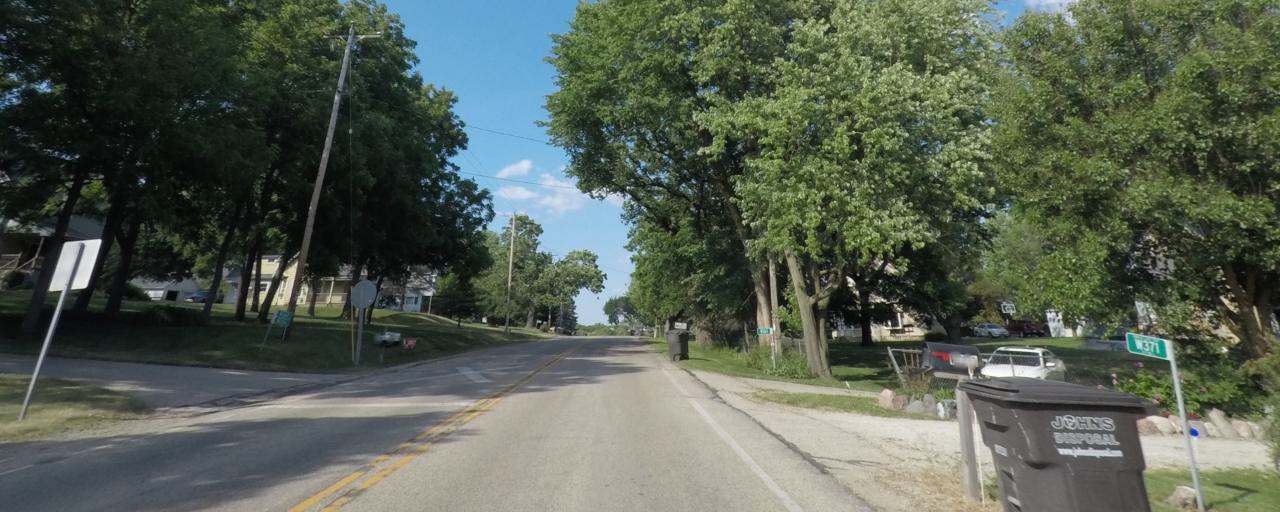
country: US
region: Wisconsin
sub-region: Walworth County
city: Potter Lake
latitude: 42.8227
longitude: -88.3205
